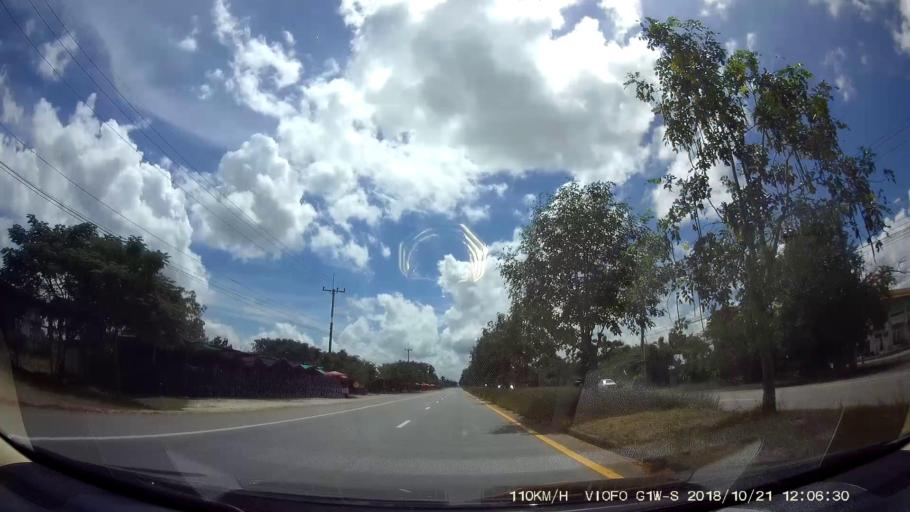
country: TH
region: Chaiyaphum
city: Chatturat
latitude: 15.4620
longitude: 101.8261
